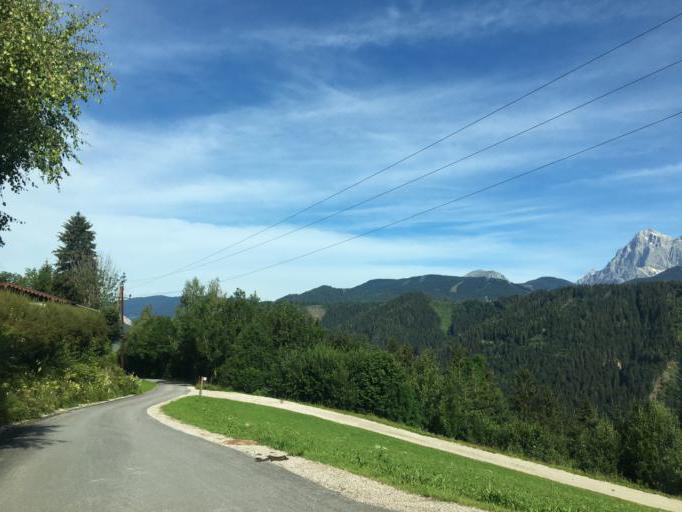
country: AT
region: Styria
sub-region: Politischer Bezirk Liezen
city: Schladming
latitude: 47.3850
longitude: 13.6641
